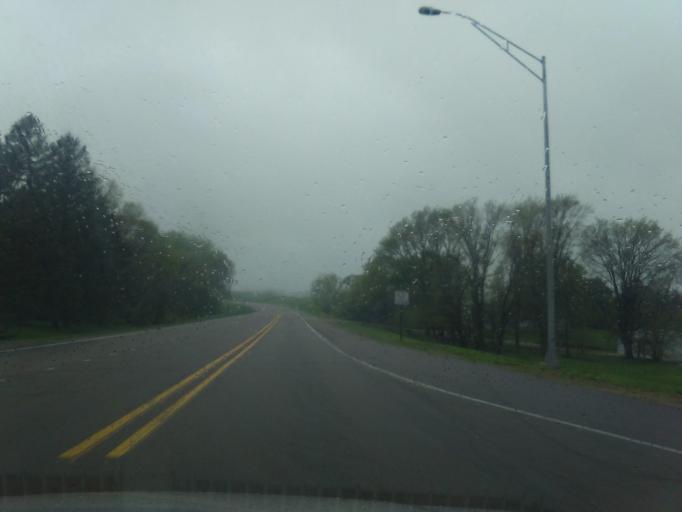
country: US
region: Nebraska
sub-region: Madison County
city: Norfolk
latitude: 42.1053
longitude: -97.3064
